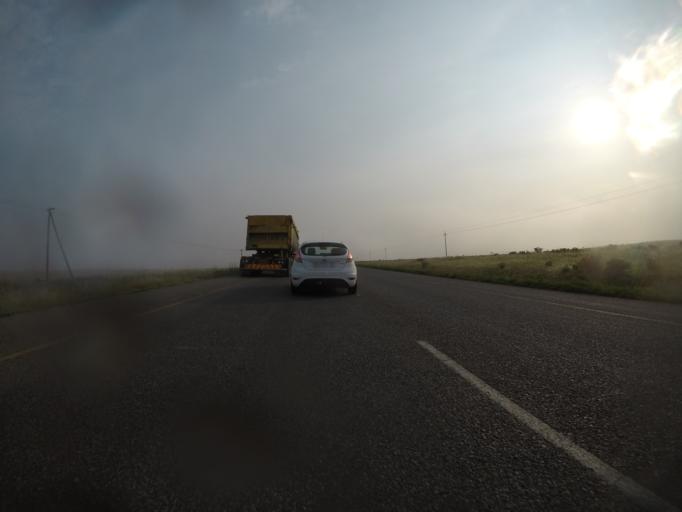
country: ZA
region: Western Cape
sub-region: West Coast District Municipality
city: Malmesbury
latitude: -33.6540
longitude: 18.7091
